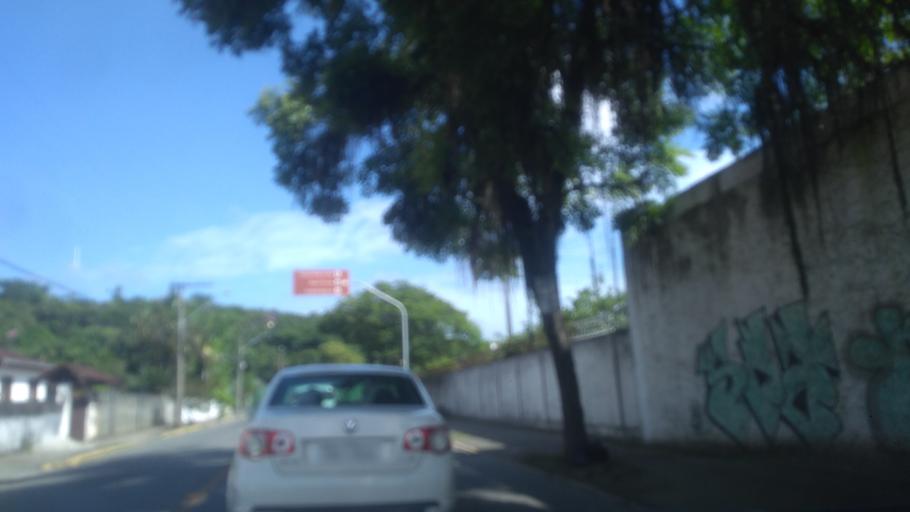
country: BR
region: Santa Catarina
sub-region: Joinville
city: Joinville
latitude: -26.3108
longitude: -48.8290
